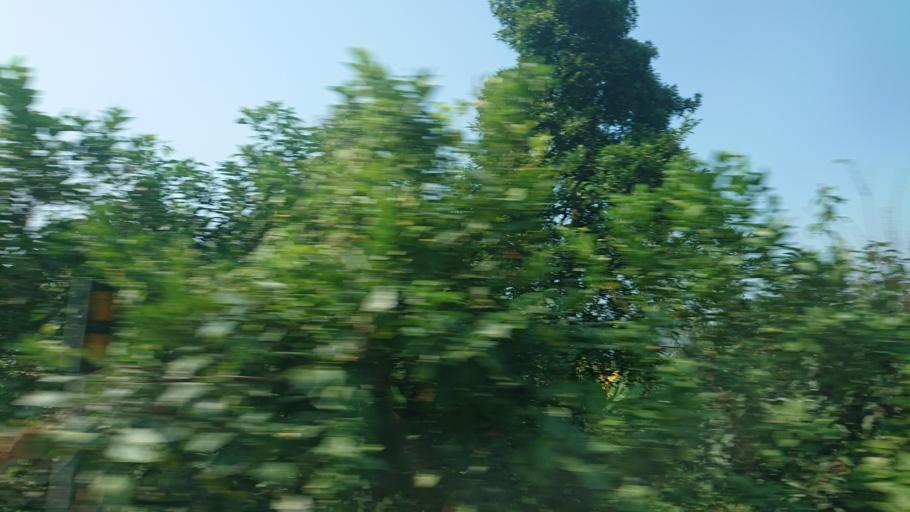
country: TW
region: Taiwan
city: Lugu
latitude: 23.6960
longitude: 120.6626
